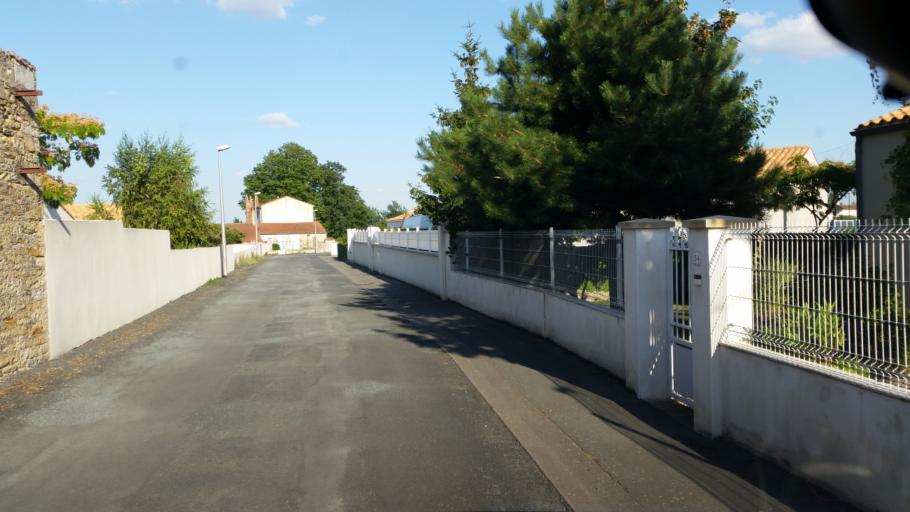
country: FR
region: Poitou-Charentes
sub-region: Departement de la Charente-Maritime
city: Marans
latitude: 46.3088
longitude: -0.9869
